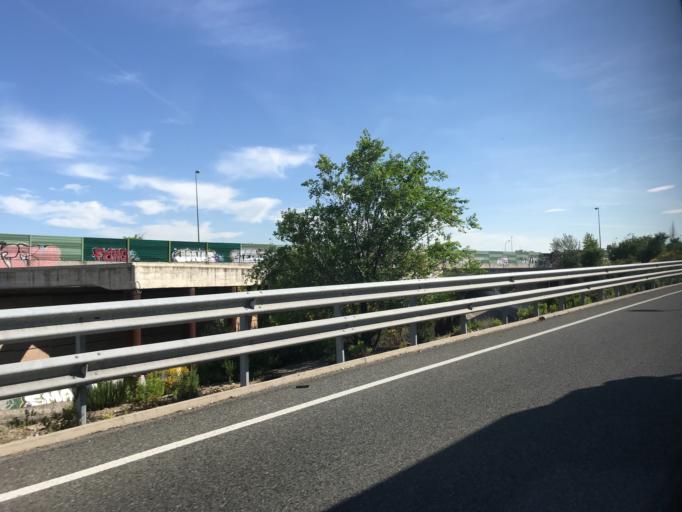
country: ES
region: Madrid
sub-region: Provincia de Madrid
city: San Blas
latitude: 40.4146
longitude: -3.6209
